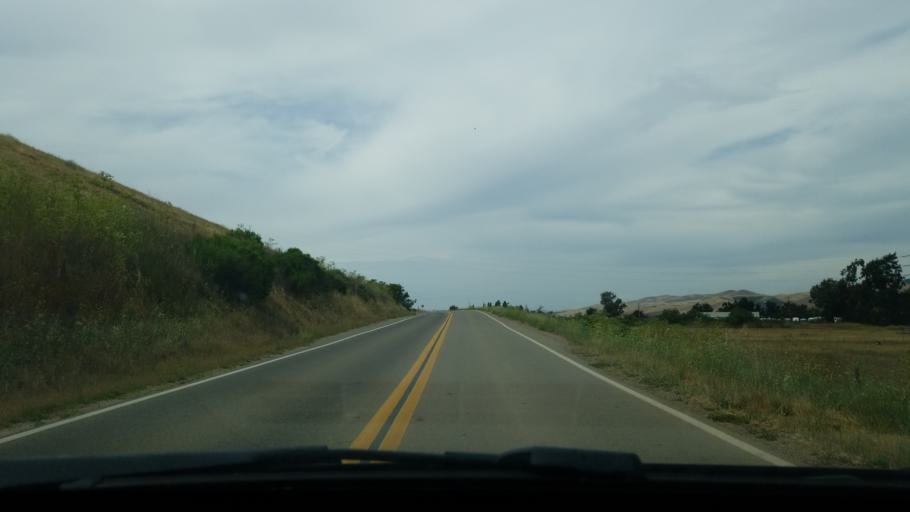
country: US
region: California
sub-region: Santa Barbara County
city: Orcutt
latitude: 34.8800
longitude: -120.3129
